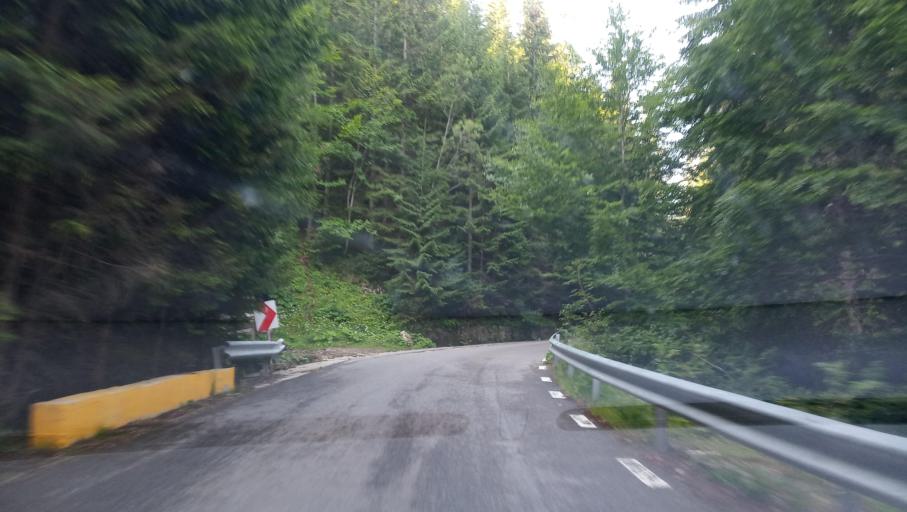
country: RO
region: Prahova
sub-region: Oras Sinaia
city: Sinaia
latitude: 45.3193
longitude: 25.4936
